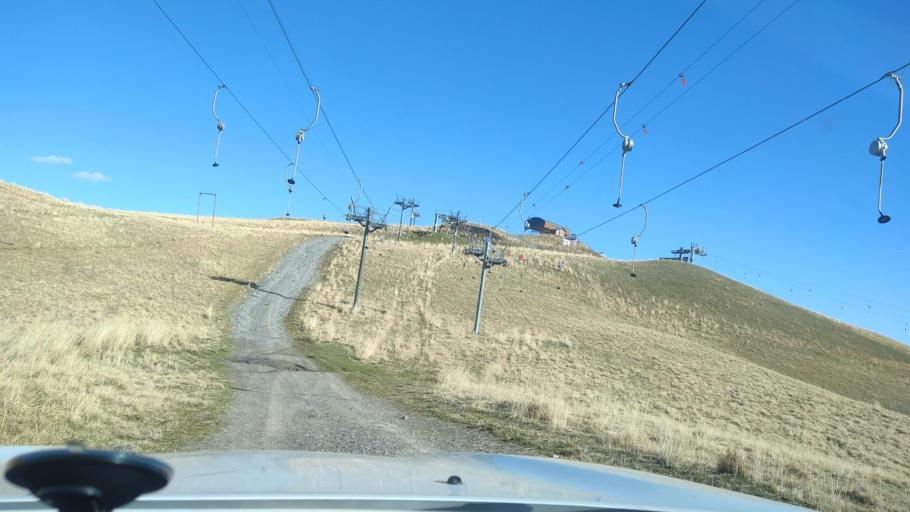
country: FR
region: Rhone-Alpes
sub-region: Departement de la Savoie
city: Saint-Etienne-de-Cuines
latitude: 45.2480
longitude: 6.2212
